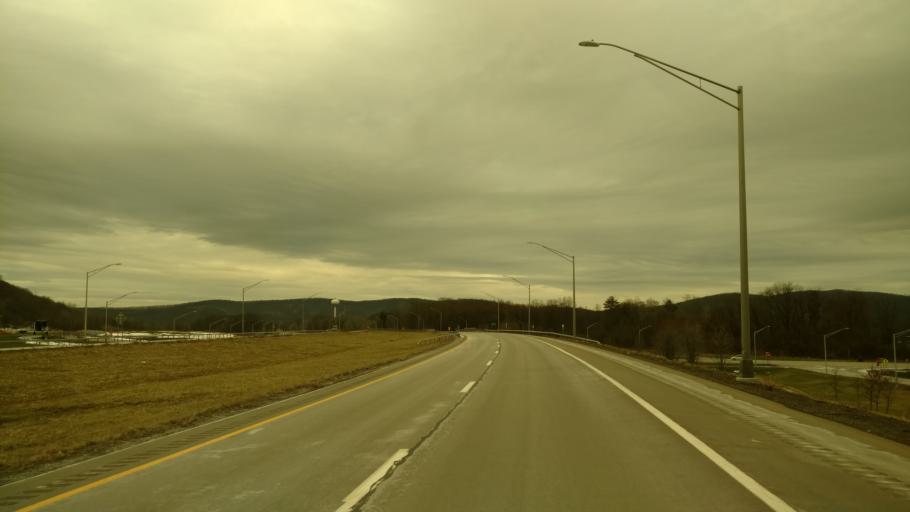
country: US
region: New York
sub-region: Cattaraugus County
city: Salamanca
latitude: 42.1543
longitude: -78.7484
